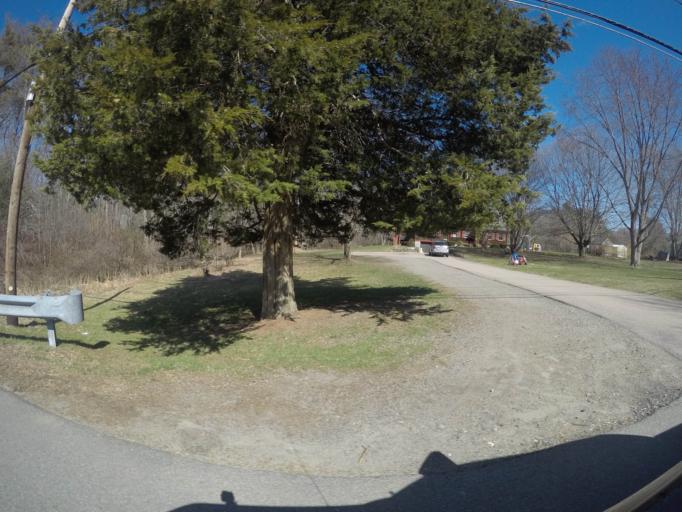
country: US
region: Massachusetts
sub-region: Bristol County
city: Easton
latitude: 42.0061
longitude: -71.0968
